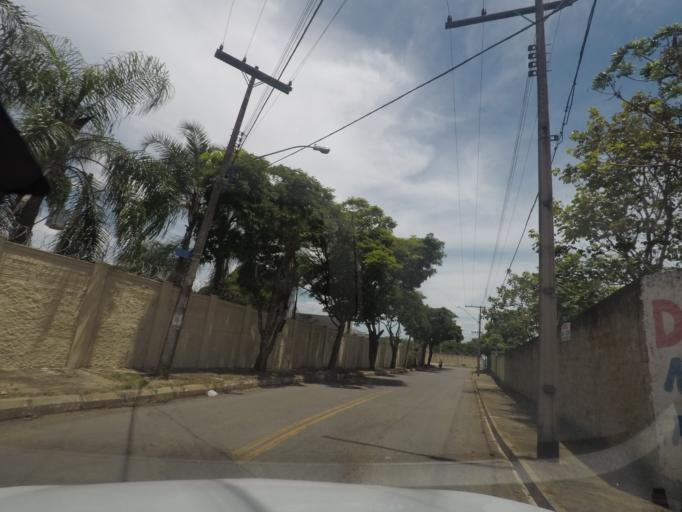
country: BR
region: Goias
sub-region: Goiania
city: Goiania
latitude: -16.6610
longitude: -49.1978
